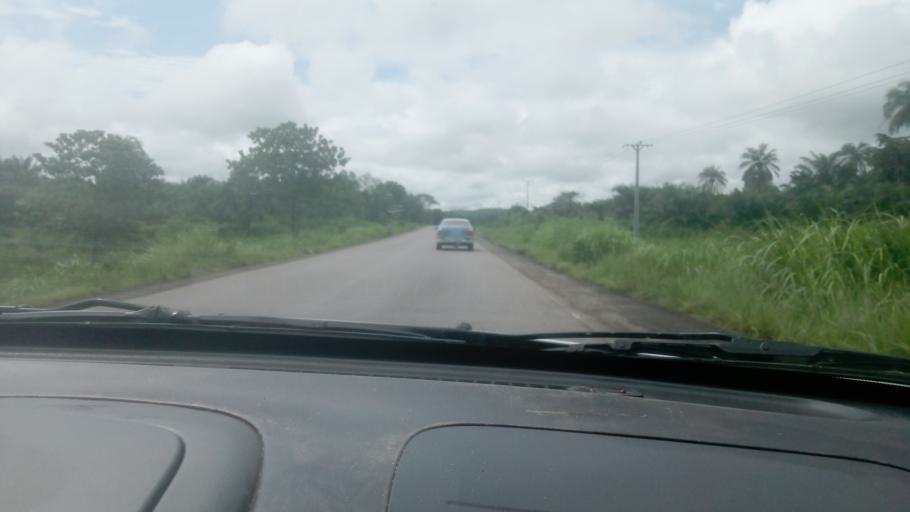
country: SL
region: Northern Province
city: Masingbi
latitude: 8.7627
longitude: -11.9785
